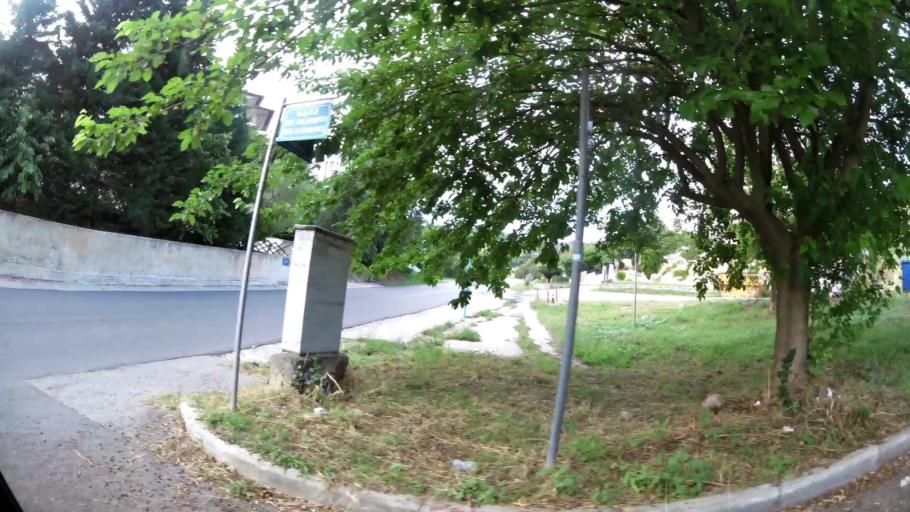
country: GR
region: Central Macedonia
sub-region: Nomos Thessalonikis
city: Pefka
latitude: 40.6609
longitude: 23.0003
